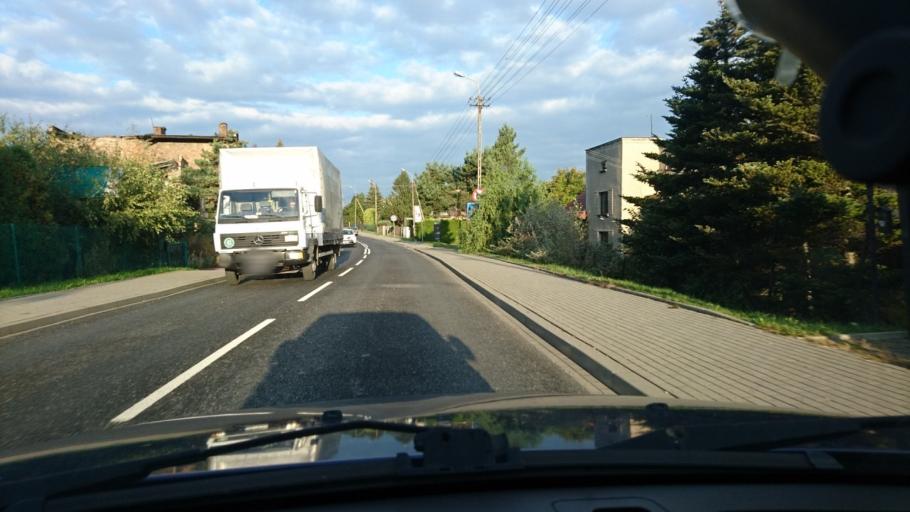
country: PL
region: Silesian Voivodeship
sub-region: Bielsko-Biala
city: Bielsko-Biala
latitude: 49.8397
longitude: 19.0675
